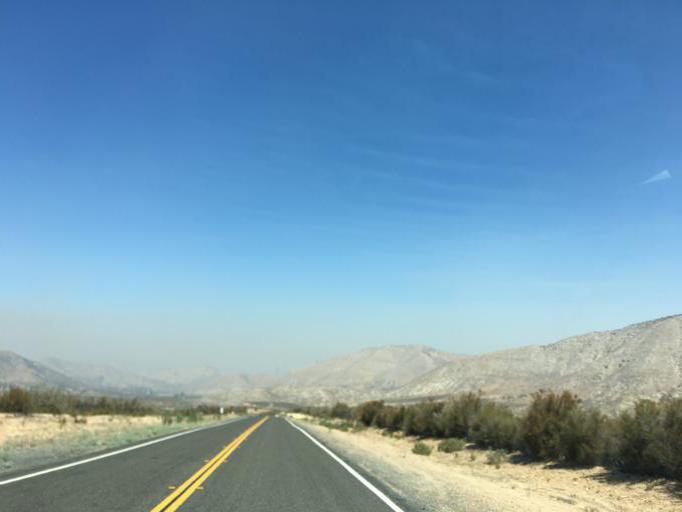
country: US
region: California
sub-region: Los Angeles County
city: Vincent
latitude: 34.4227
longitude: -118.1013
